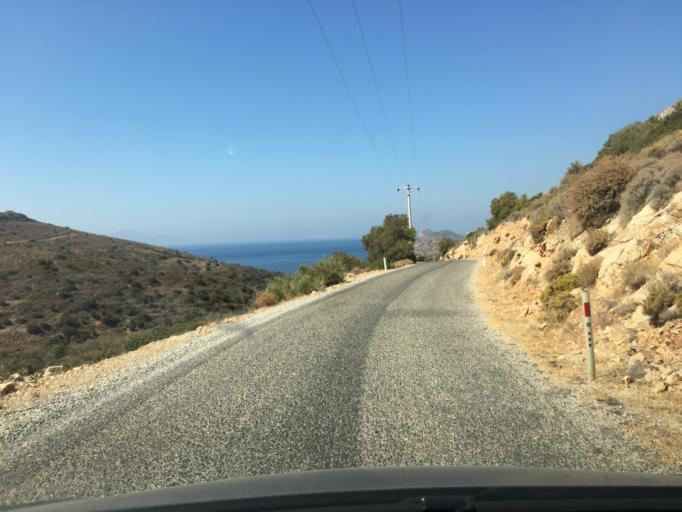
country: GR
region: South Aegean
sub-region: Nomos Dodekanisou
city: Megalo Chorio
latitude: 36.6789
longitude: 27.4198
